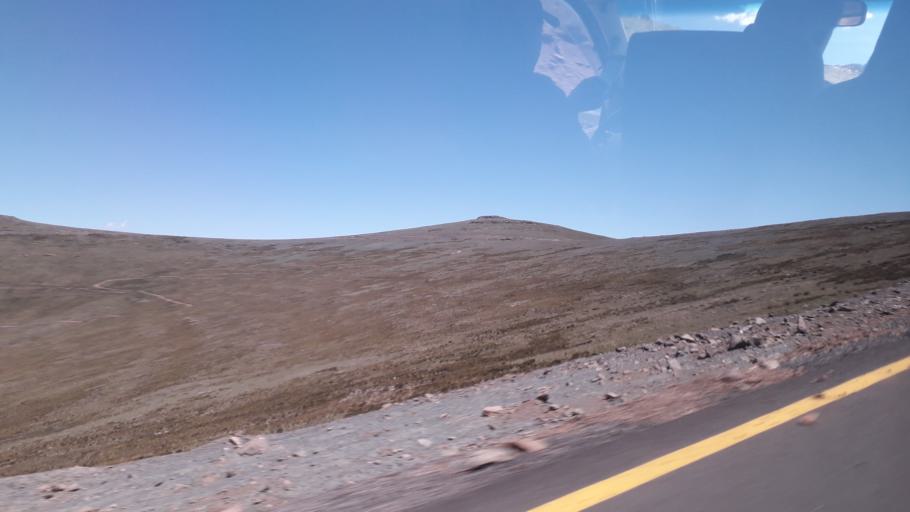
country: ZA
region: Orange Free State
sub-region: Thabo Mofutsanyana District Municipality
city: Phuthaditjhaba
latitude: -28.8190
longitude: 28.7347
